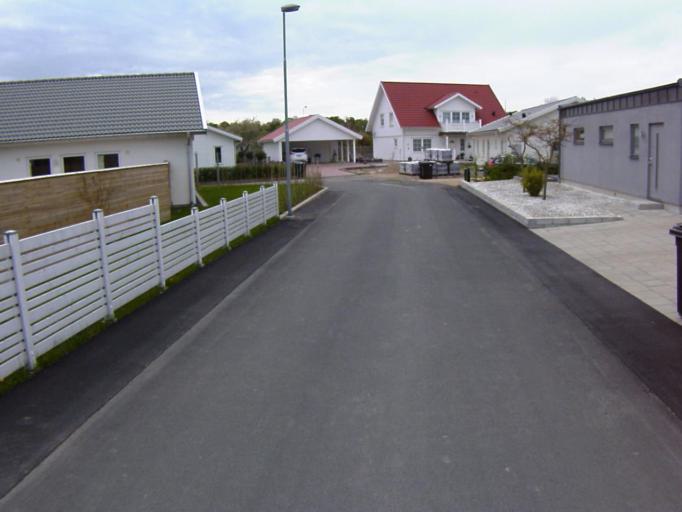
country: SE
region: Skane
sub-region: Kristianstads Kommun
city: Kristianstad
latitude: 56.0194
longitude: 14.1953
